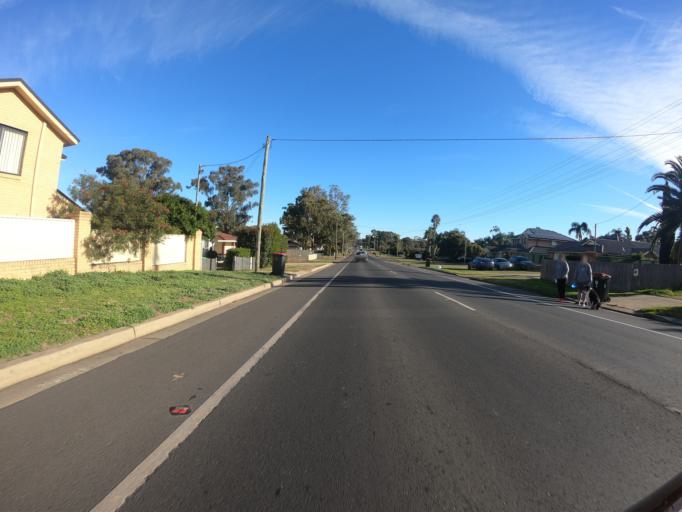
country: AU
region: New South Wales
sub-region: Hawkesbury
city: South Windsor
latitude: -33.6263
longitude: 150.7975
